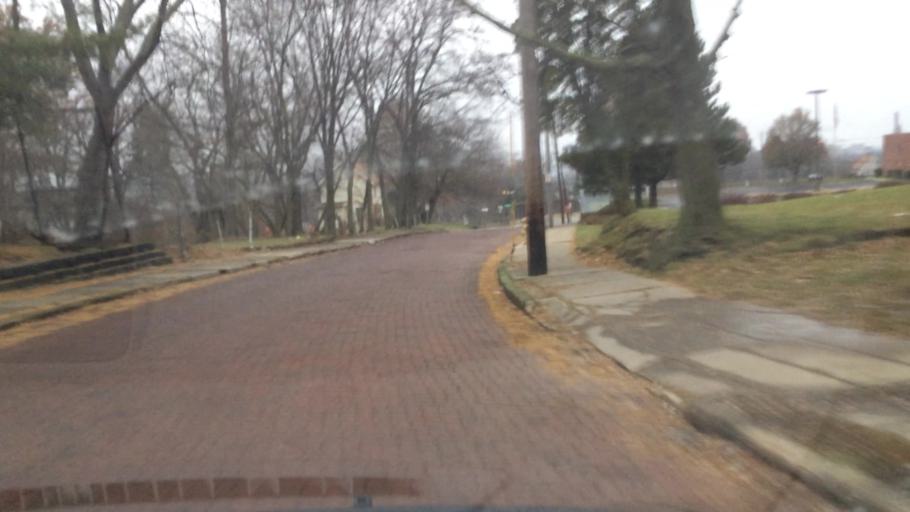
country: US
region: Ohio
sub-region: Summit County
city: Akron
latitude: 41.0605
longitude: -81.5345
